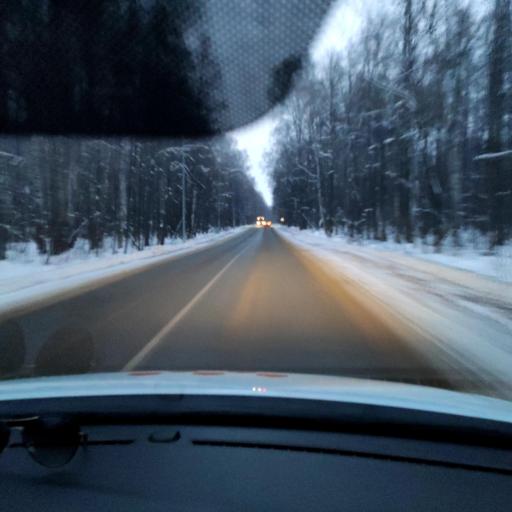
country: RU
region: Tatarstan
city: Vysokaya Gora
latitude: 55.9316
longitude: 49.1652
